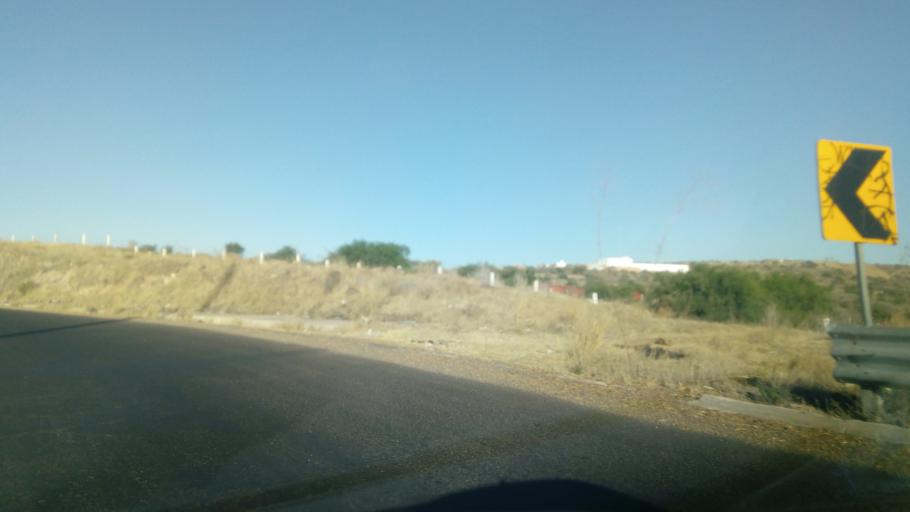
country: MX
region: Durango
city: Victoria de Durango
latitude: 24.0788
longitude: -104.6218
